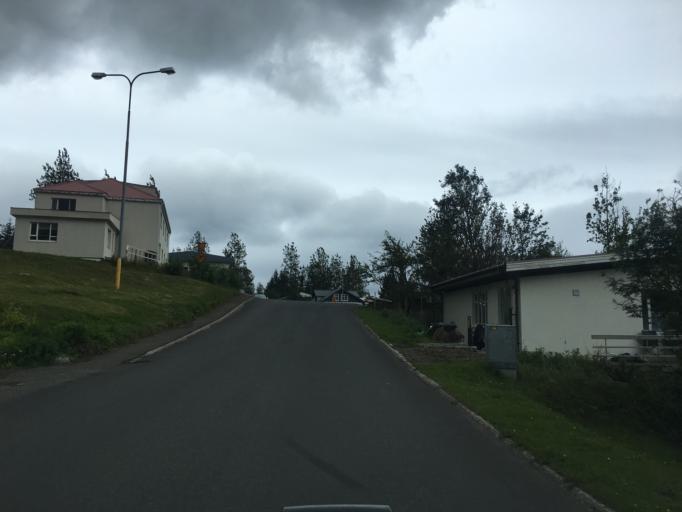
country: IS
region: East
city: Neskaupstadur
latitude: 65.1483
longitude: -13.6941
